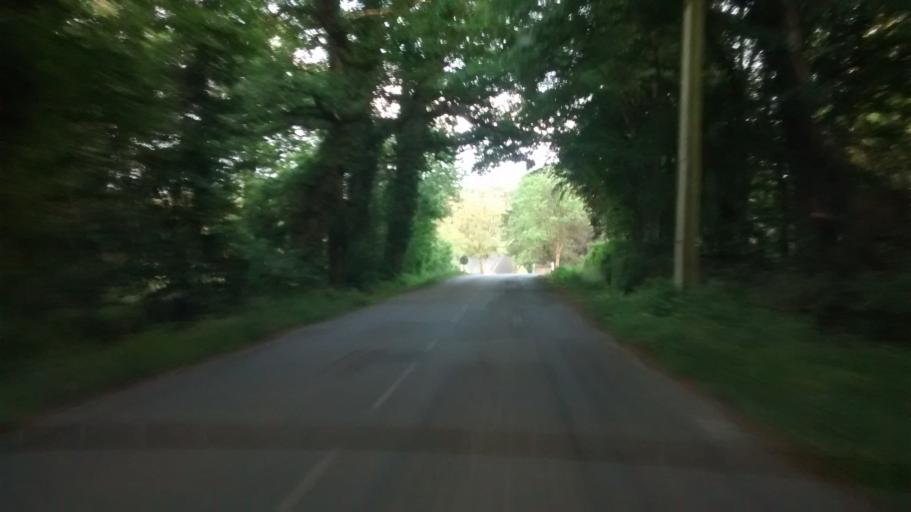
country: FR
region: Brittany
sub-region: Departement du Morbihan
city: Beignon
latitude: 47.9952
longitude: -2.1424
